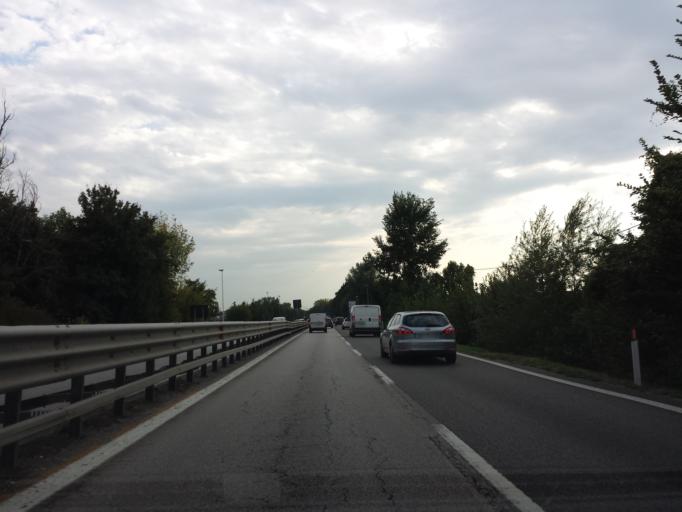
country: IT
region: Veneto
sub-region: Provincia di Padova
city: Padova
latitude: 45.4193
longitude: 11.8556
